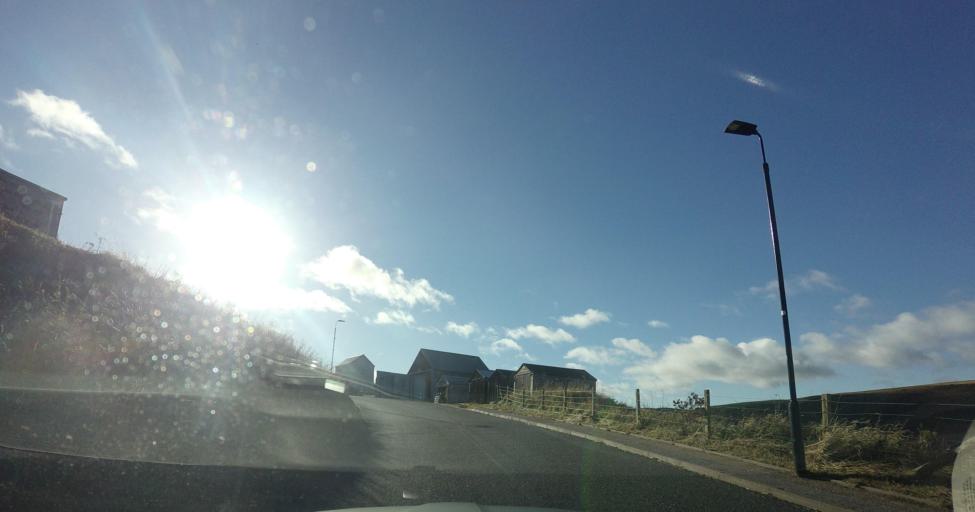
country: GB
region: Scotland
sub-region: Aberdeenshire
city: Macduff
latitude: 57.6709
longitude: -2.3370
